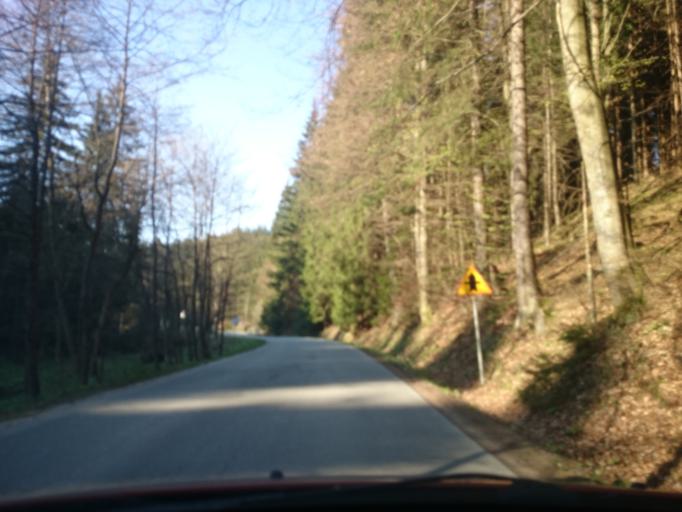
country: PL
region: Lower Silesian Voivodeship
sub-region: Powiat klodzki
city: Duszniki-Zdroj
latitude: 50.3676
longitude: 16.3922
